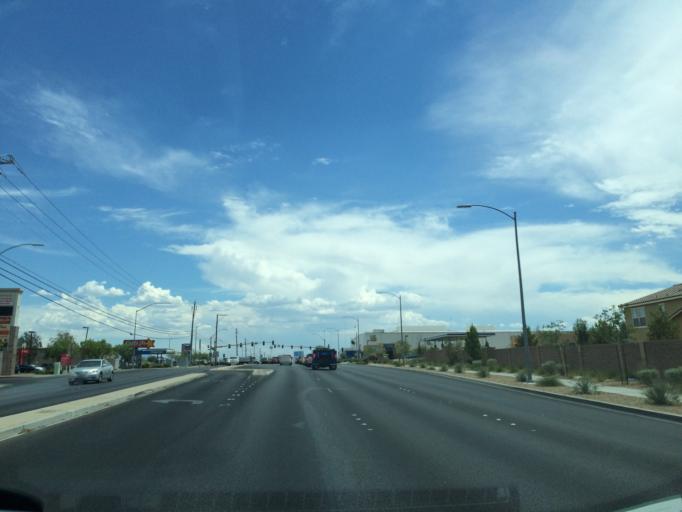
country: US
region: Nevada
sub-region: Clark County
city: North Las Vegas
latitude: 36.2197
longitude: -115.1614
